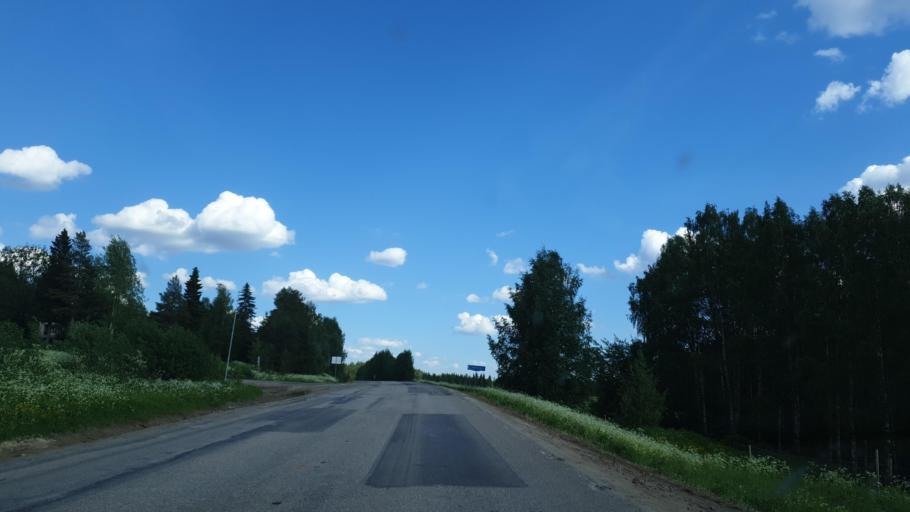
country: SE
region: Norrbotten
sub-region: Alvsbyns Kommun
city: AElvsbyn
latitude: 65.8542
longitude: 20.4355
